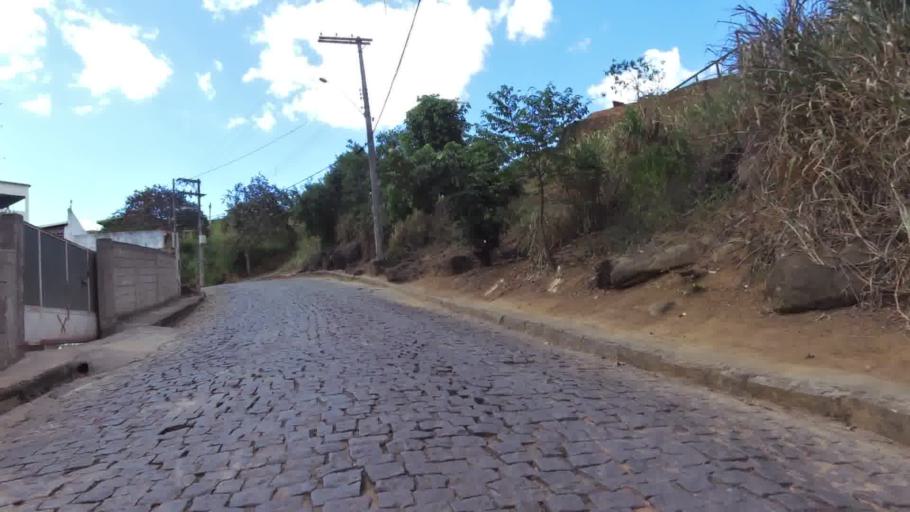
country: BR
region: Espirito Santo
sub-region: Rio Novo Do Sul
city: Rio Novo do Sul
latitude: -20.8651
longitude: -40.9446
